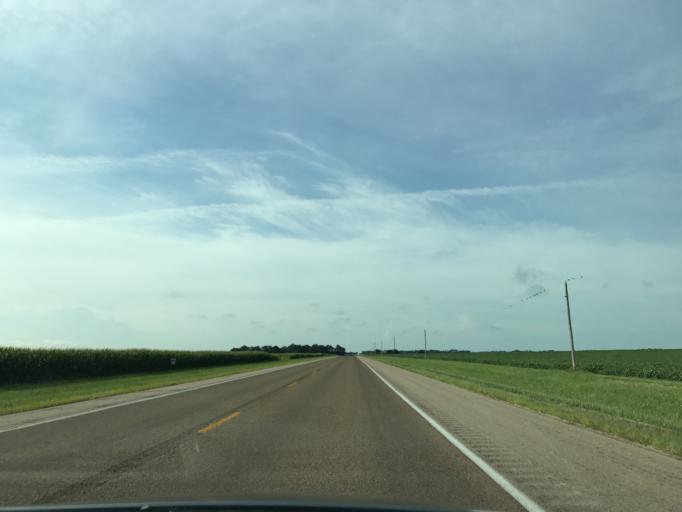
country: US
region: Nebraska
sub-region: Butler County
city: David City
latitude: 41.1527
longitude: -97.1006
